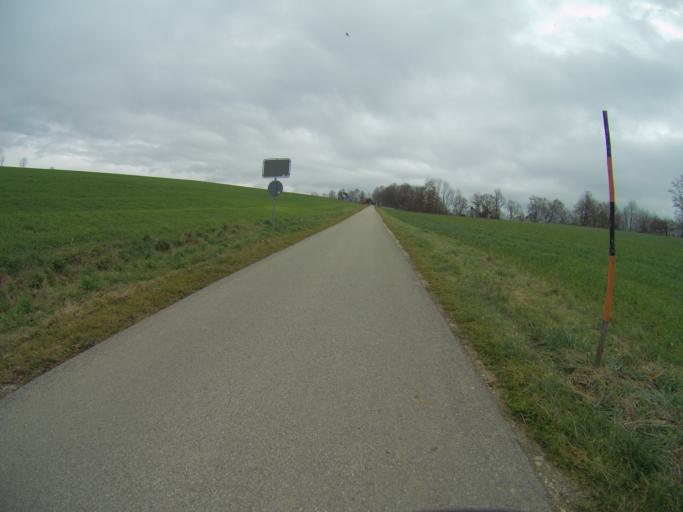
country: DE
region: Bavaria
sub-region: Upper Bavaria
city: Marzling
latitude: 48.4084
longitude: 11.8213
